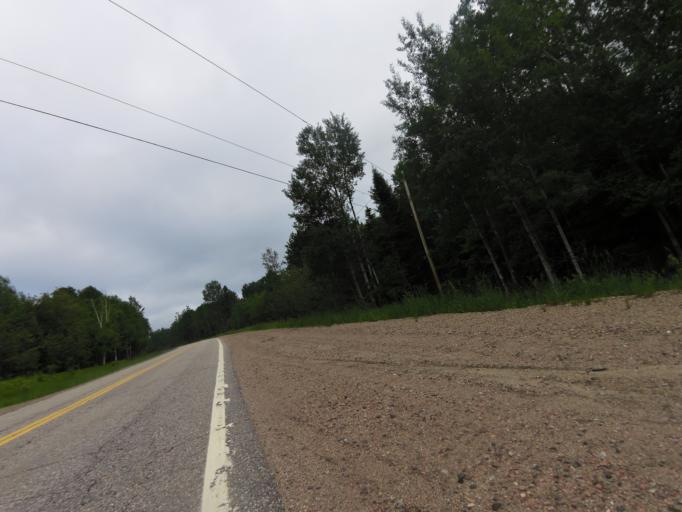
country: CA
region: Quebec
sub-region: Outaouais
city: Shawville
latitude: 45.9106
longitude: -76.3139
